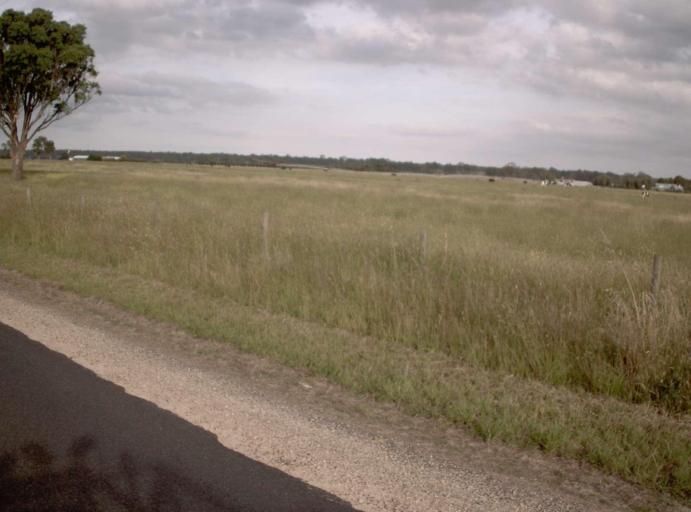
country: AU
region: Victoria
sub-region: Wellington
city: Sale
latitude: -37.8624
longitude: 147.0336
